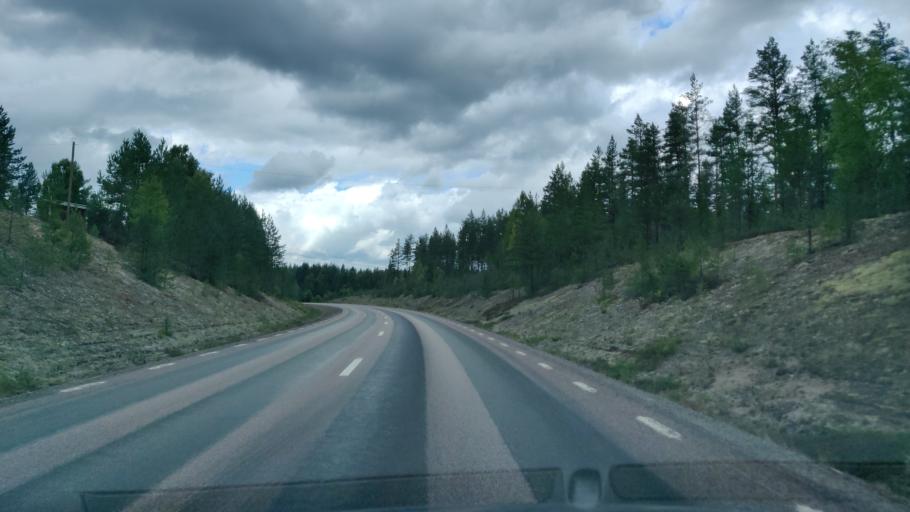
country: SE
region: Vaermland
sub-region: Torsby Kommun
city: Torsby
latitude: 60.5288
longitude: 13.1301
